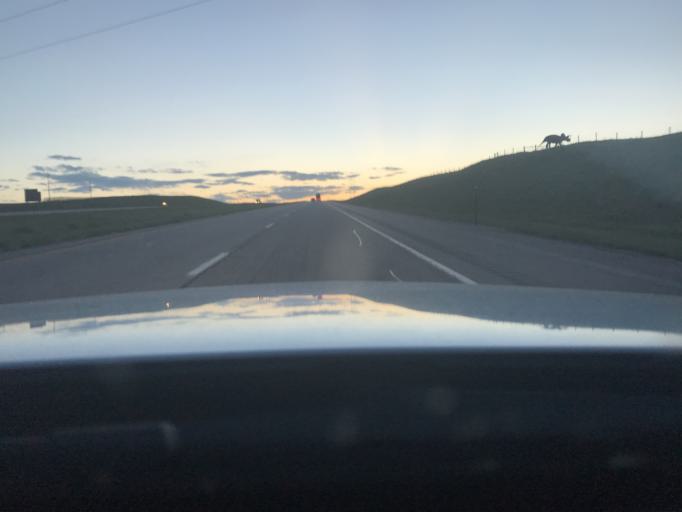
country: US
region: Wyoming
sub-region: Converse County
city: Glenrock
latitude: 42.8275
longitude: -105.8231
